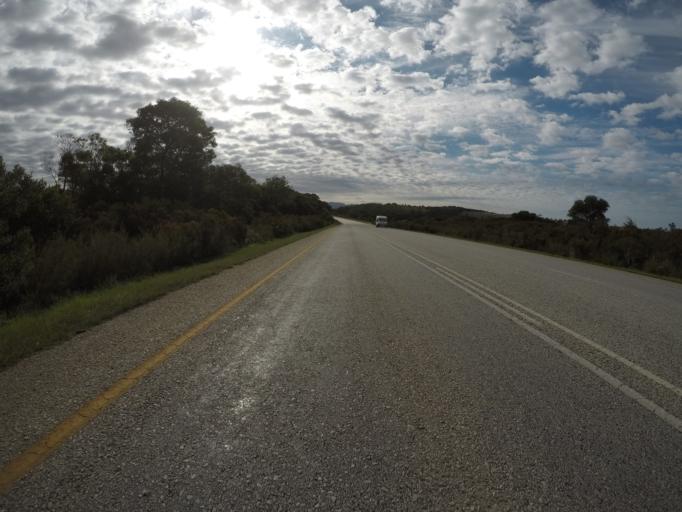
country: ZA
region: Eastern Cape
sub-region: Cacadu District Municipality
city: Kruisfontein
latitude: -34.0425
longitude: 24.5434
